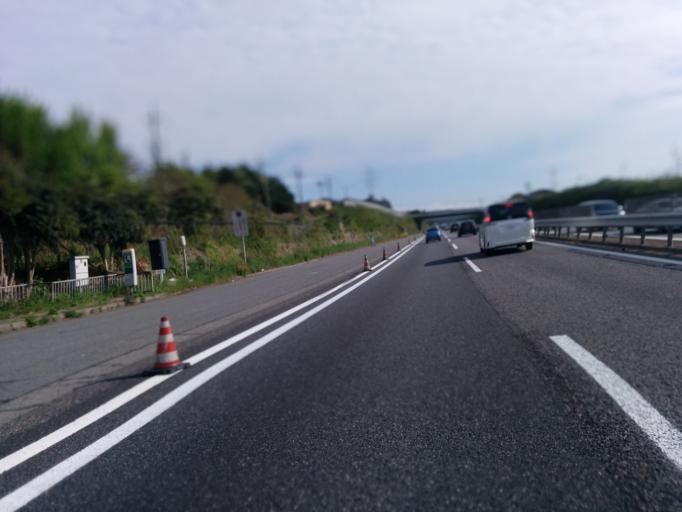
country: JP
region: Mie
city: Komono
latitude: 34.9671
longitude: 136.5092
